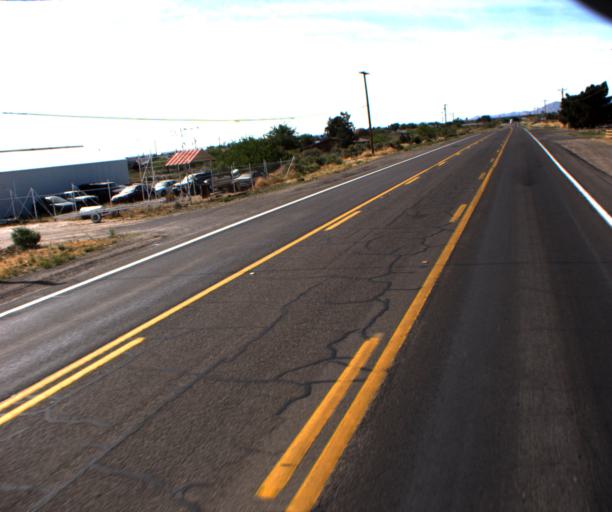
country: US
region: Arizona
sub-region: Graham County
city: Swift Trail Junction
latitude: 32.7423
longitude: -109.7164
